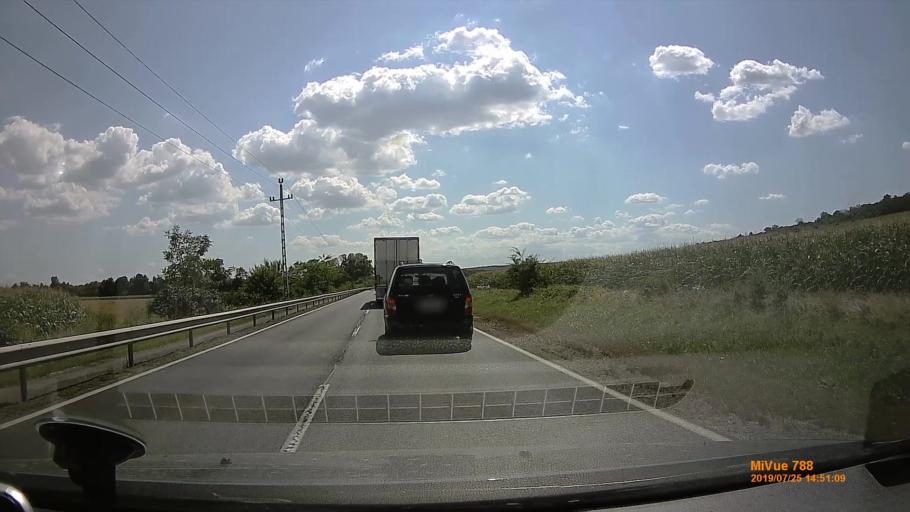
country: HU
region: Borsod-Abauj-Zemplen
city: Szikszo
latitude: 48.2169
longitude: 20.9456
